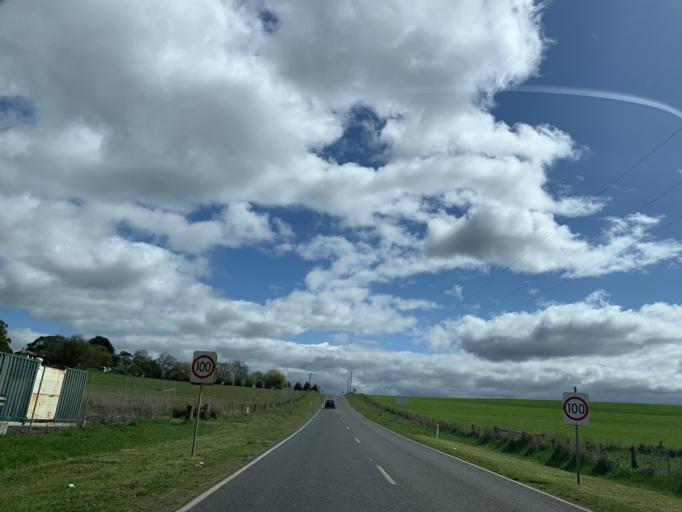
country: AU
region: Victoria
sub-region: Whittlesea
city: Whittlesea
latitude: -37.2804
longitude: 144.9420
